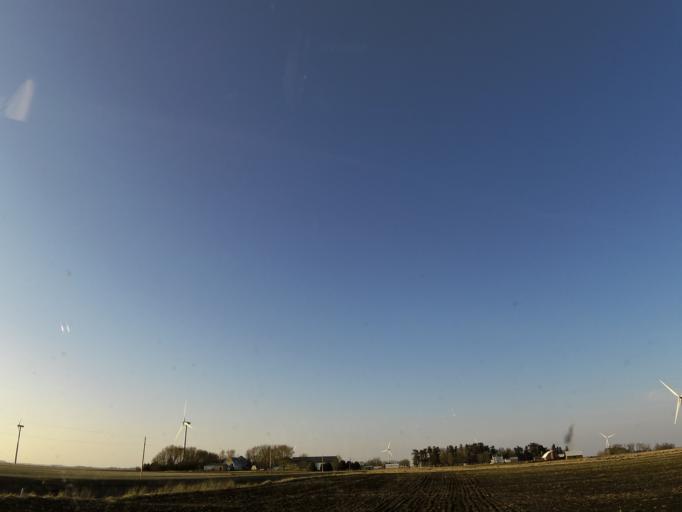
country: US
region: Iowa
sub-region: Worth County
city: Northwood
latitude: 43.4008
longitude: -93.1237
